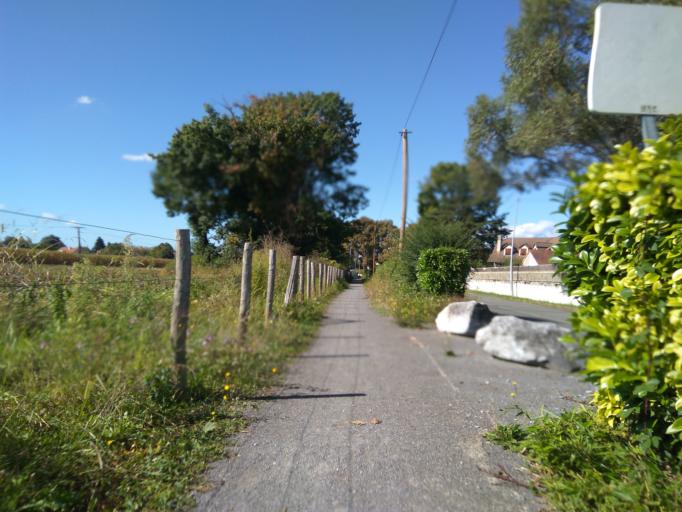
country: FR
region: Aquitaine
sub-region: Departement des Pyrenees-Atlantiques
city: Idron
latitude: 43.3016
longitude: -0.3233
